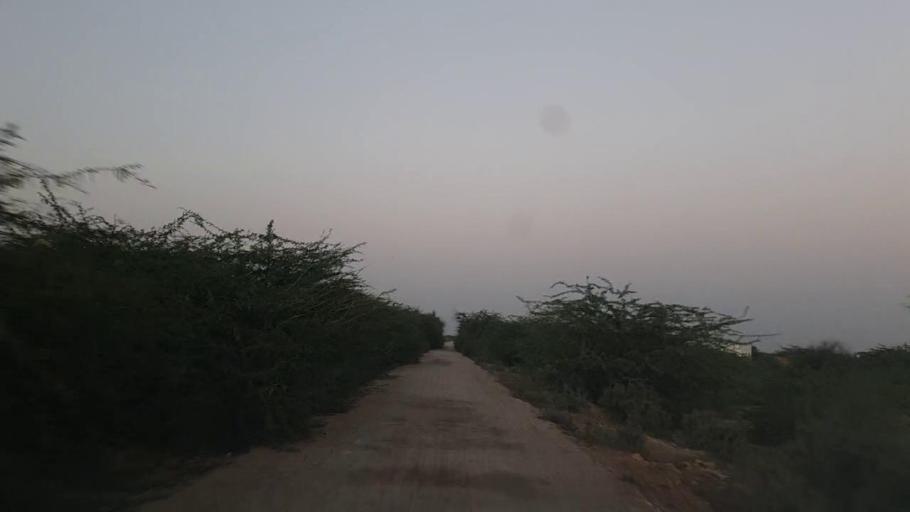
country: PK
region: Sindh
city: Naukot
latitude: 24.7587
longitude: 69.2887
